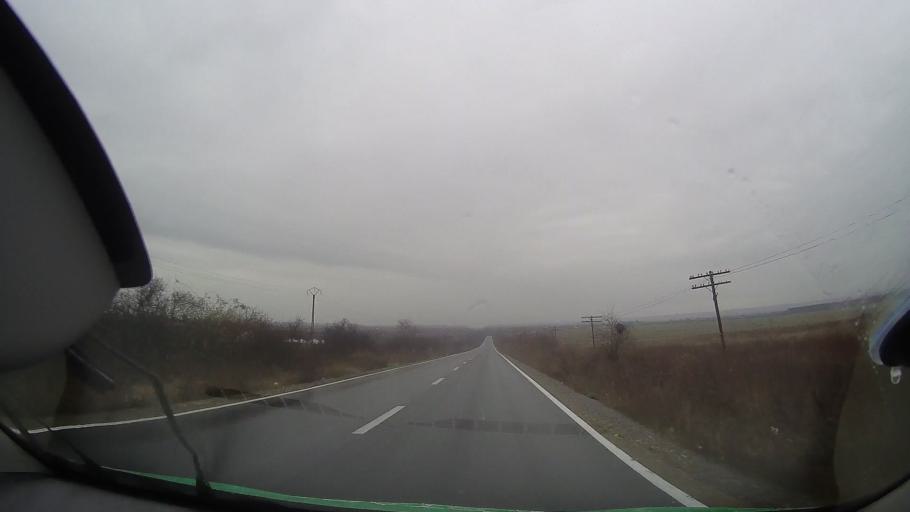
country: RO
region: Bihor
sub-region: Comuna Olcea
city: Calacea
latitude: 46.7182
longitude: 21.9526
